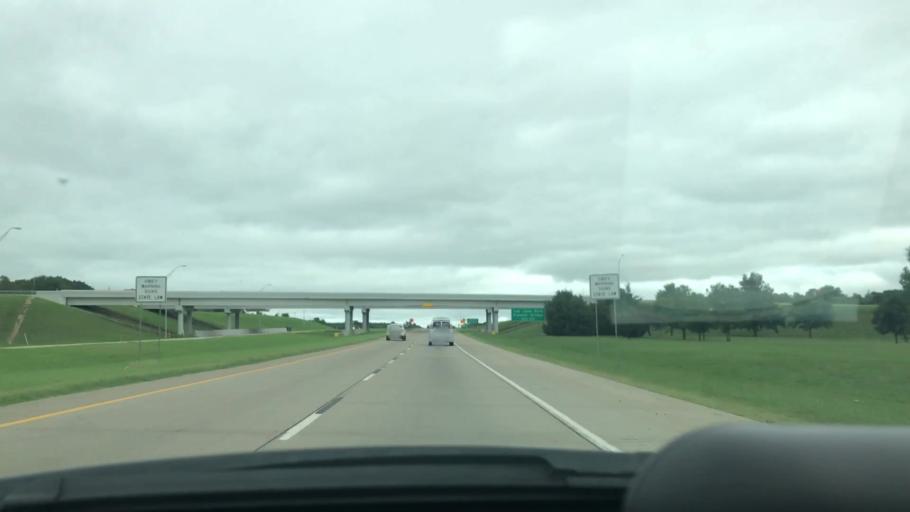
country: US
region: Texas
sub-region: Grayson County
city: Denison
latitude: 33.7192
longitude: -96.5852
